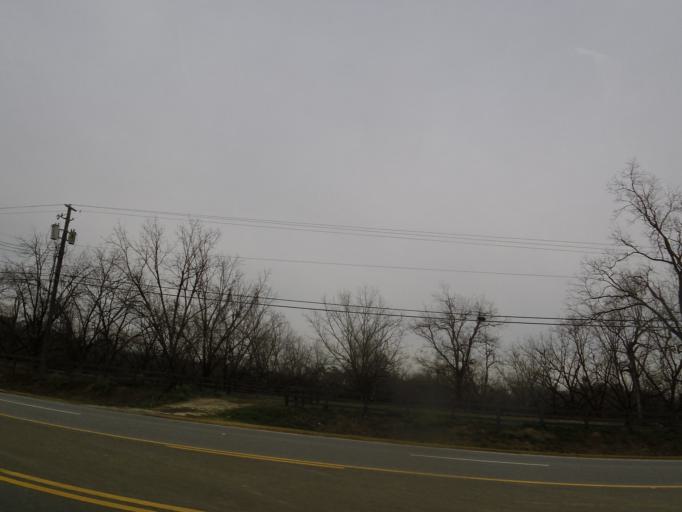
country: US
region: Georgia
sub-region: Grady County
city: Cairo
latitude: 30.8743
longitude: -84.1619
